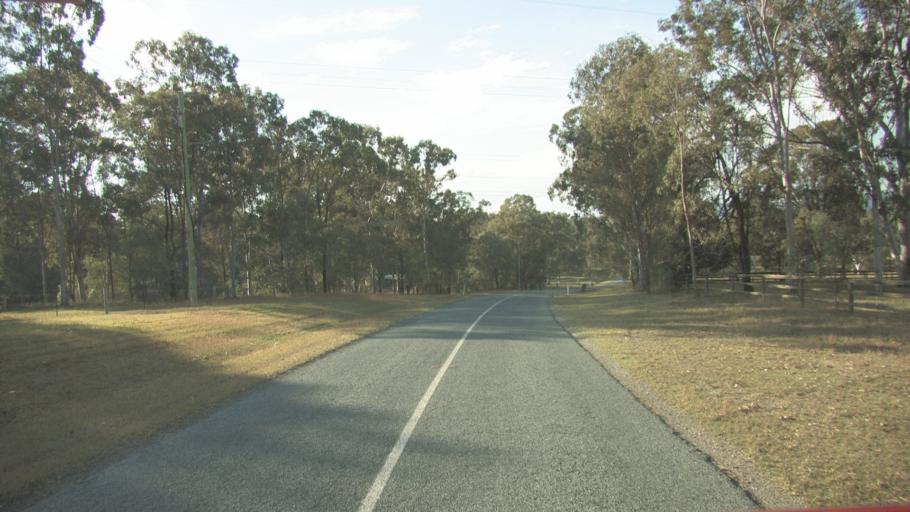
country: AU
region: Queensland
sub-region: Gold Coast
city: Ormeau Hills
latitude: -27.8324
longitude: 153.1700
